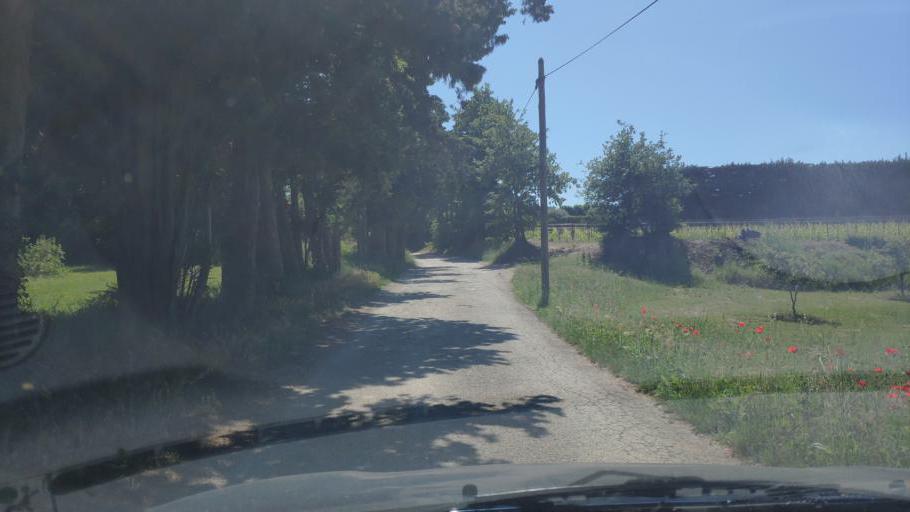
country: FR
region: Provence-Alpes-Cote d'Azur
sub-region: Departement du Vaucluse
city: Carpentras
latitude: 44.0789
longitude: 5.0555
